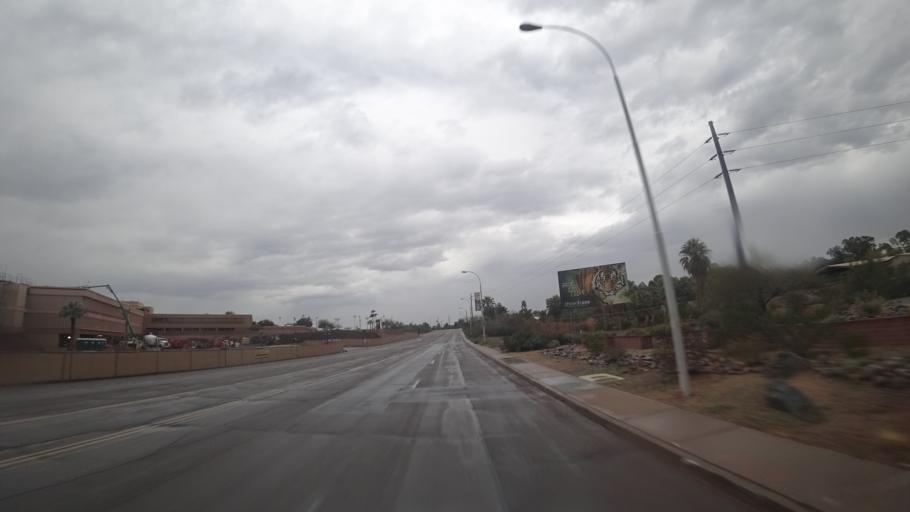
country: US
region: Arizona
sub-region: Maricopa County
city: Tempe Junction
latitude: 33.4461
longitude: -111.9499
